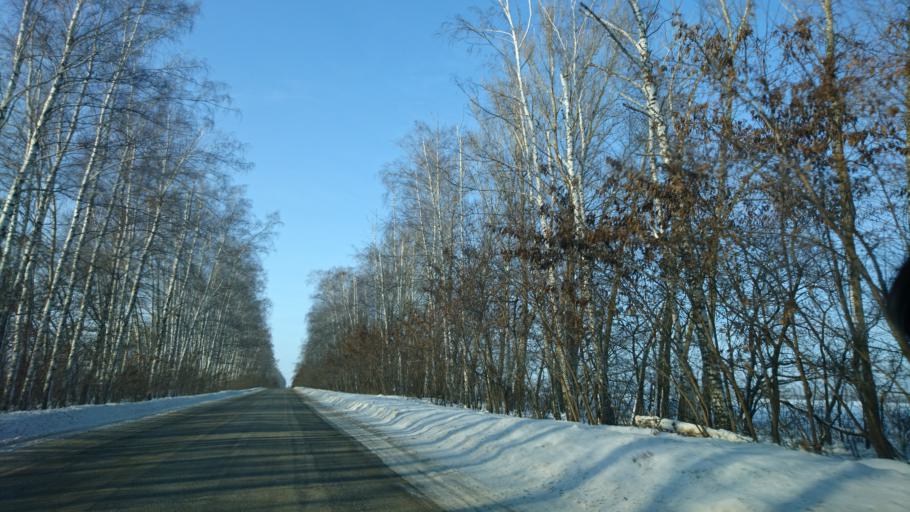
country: RU
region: Belgorod
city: Severnyy
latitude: 50.7280
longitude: 36.5479
